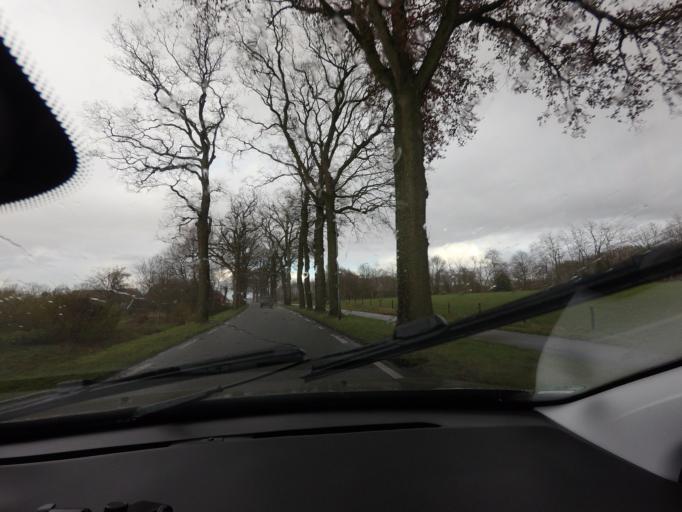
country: NL
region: Drenthe
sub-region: Gemeente Aa en Hunze
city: Anloo
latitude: 53.0292
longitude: 6.8027
